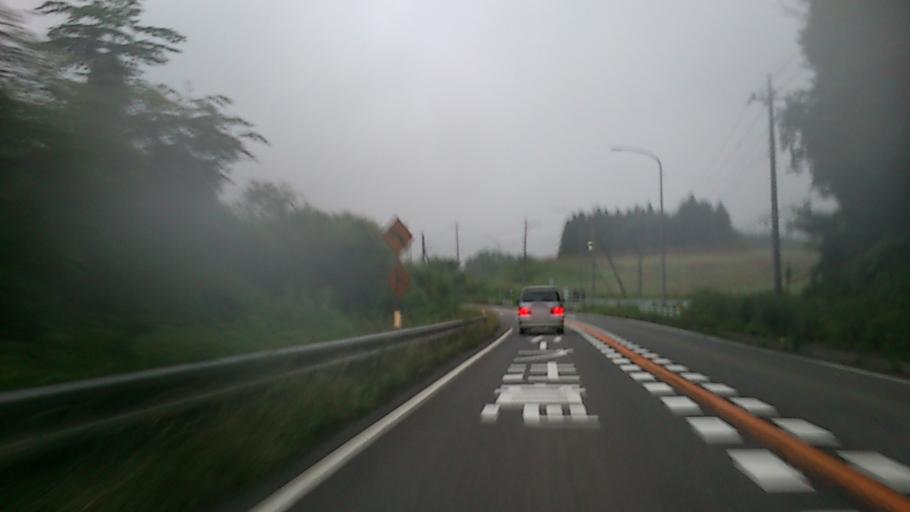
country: JP
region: Tochigi
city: Kuroiso
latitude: 37.0970
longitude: 140.1358
